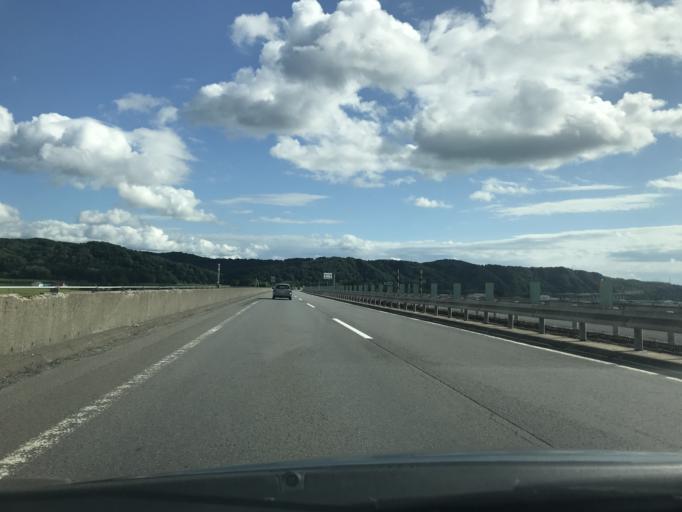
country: JP
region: Hokkaido
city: Takikawa
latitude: 43.5620
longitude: 141.9546
